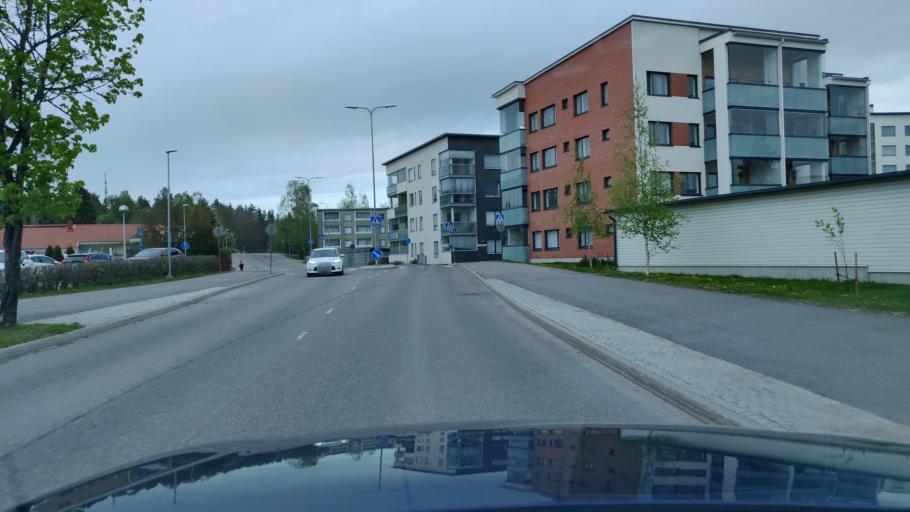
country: FI
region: Uusimaa
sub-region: Helsinki
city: Nurmijaervi
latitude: 60.3829
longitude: 24.7530
